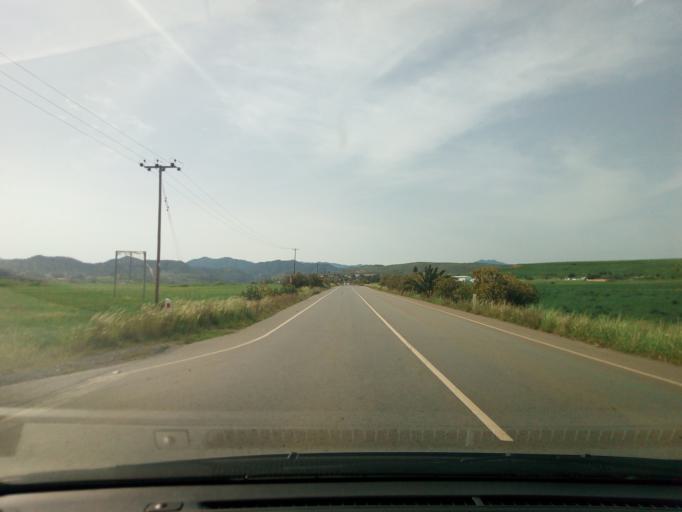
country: CY
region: Lefkosia
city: Klirou
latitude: 35.0348
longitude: 33.1703
